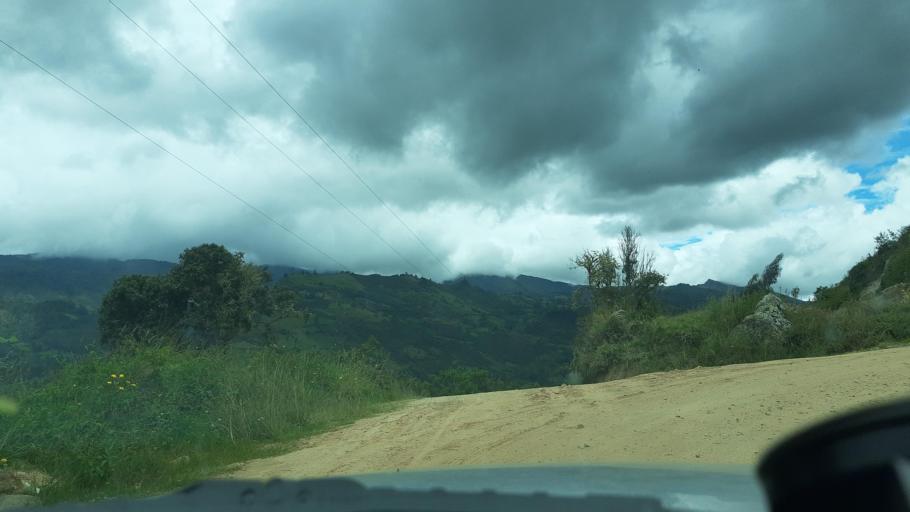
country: CO
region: Cundinamarca
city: Umbita
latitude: 5.2190
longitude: -73.4494
